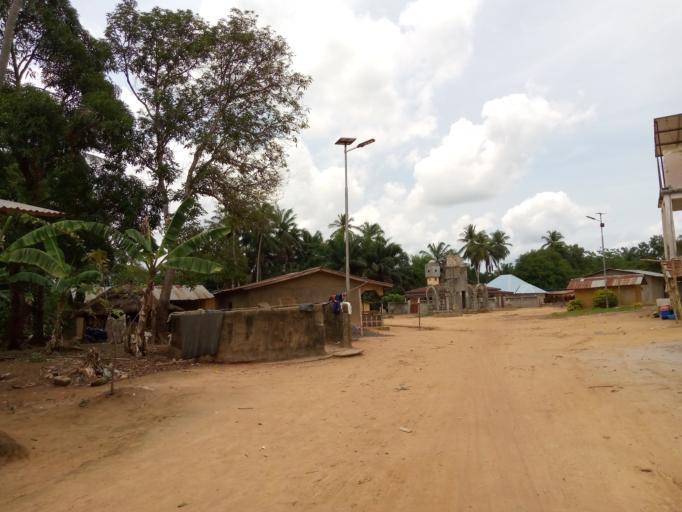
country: SL
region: Western Area
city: Waterloo
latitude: 8.3358
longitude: -12.9418
